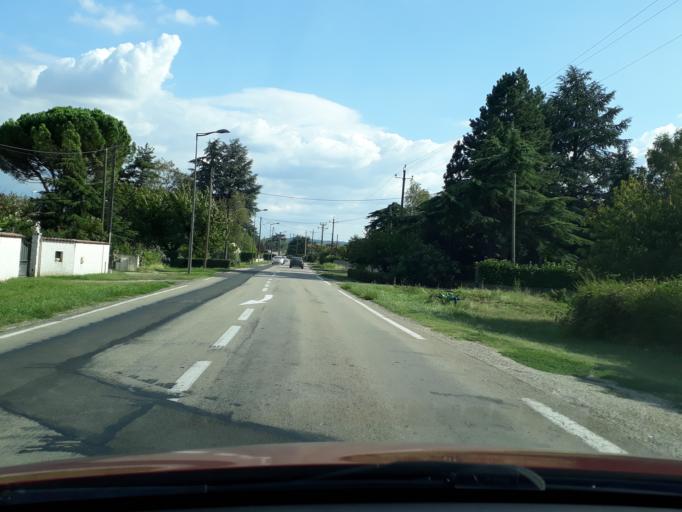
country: FR
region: Rhone-Alpes
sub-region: Departement de la Loire
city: Saint-Pierre-de-Boeuf
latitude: 45.3581
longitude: 4.7561
